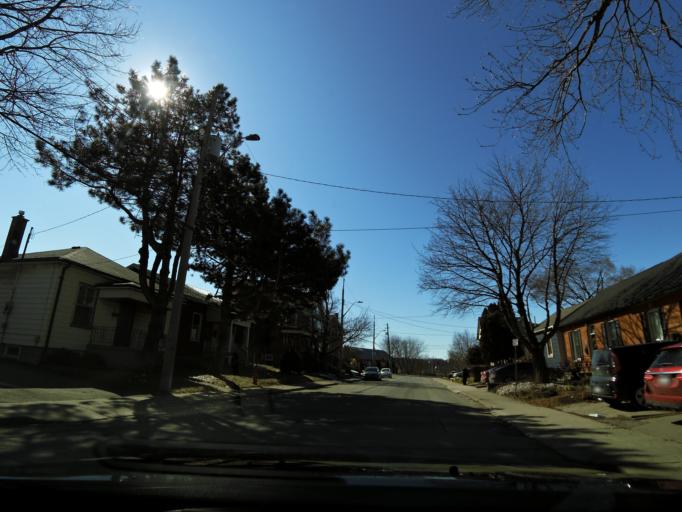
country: CA
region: Ontario
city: Hamilton
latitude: 43.2723
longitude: -79.8652
